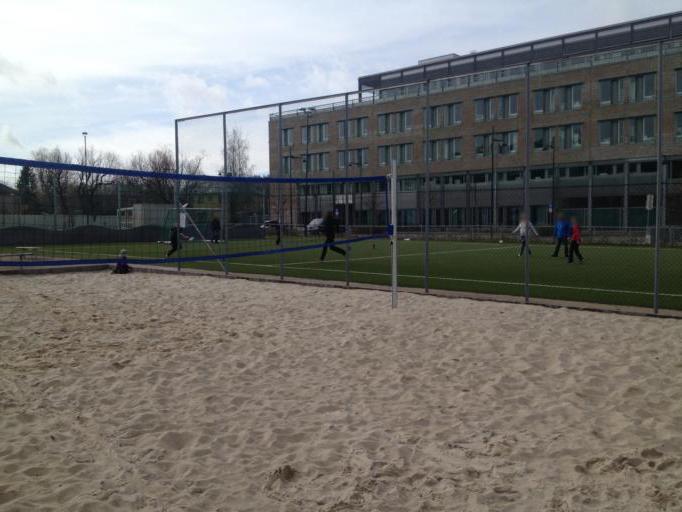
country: NO
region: Sor-Trondelag
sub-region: Trondheim
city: Trondheim
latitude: 63.4195
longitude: 10.3930
